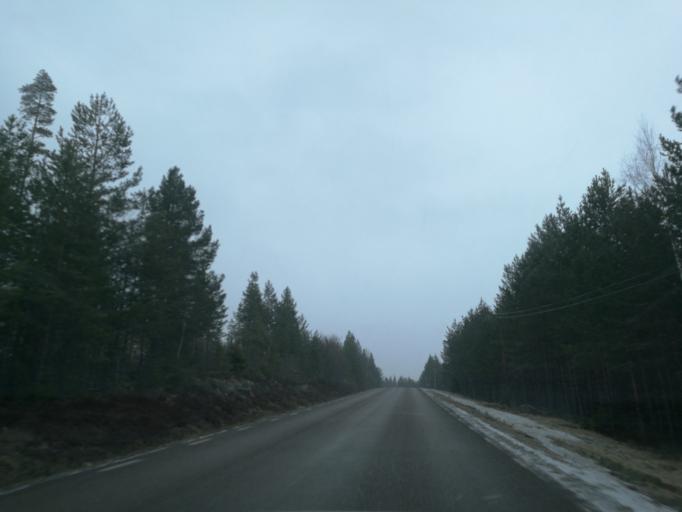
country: NO
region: Hedmark
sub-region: Asnes
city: Flisa
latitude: 60.6962
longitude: 12.5536
